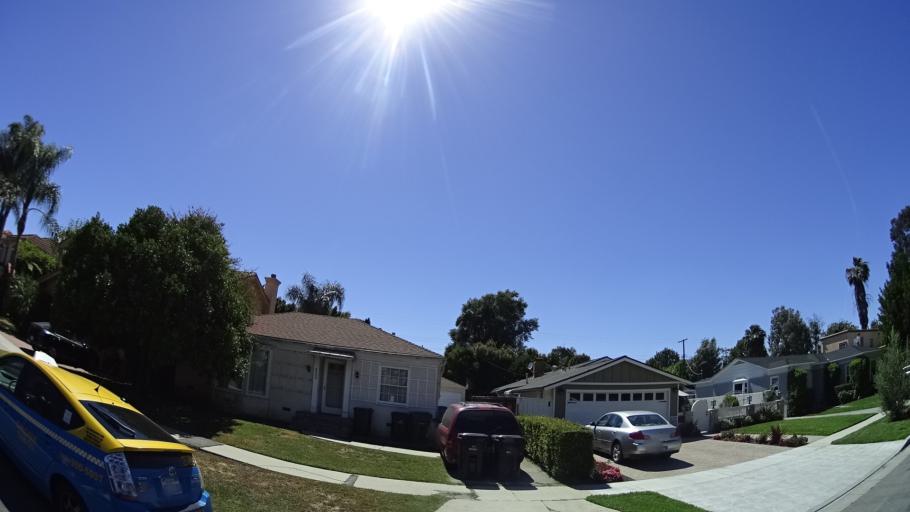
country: US
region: California
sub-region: Los Angeles County
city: Sherman Oaks
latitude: 34.1540
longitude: -118.4520
